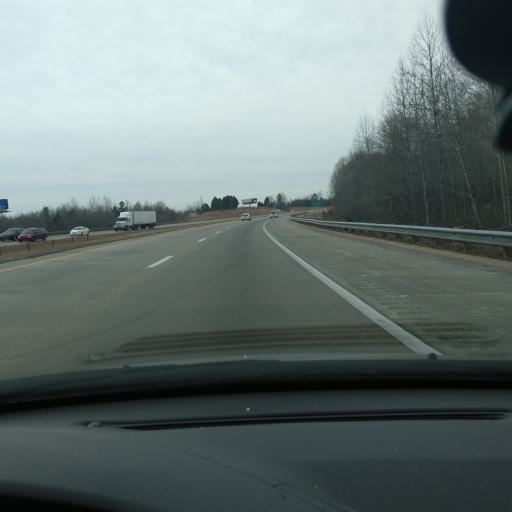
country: US
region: North Carolina
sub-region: Davidson County
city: Welcome
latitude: 35.8786
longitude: -80.2324
